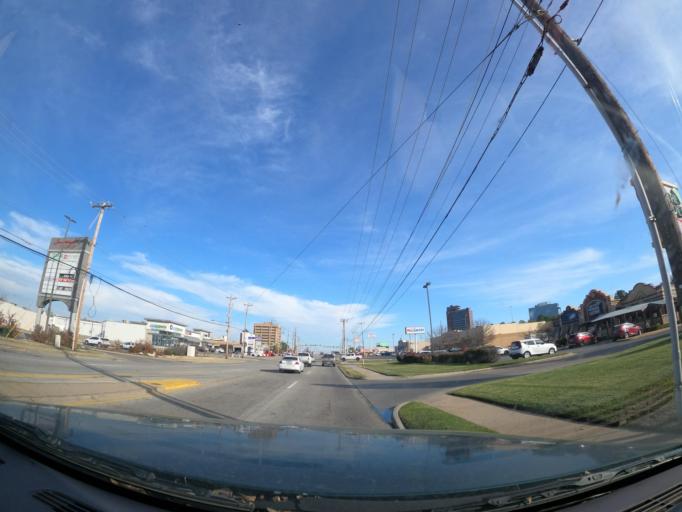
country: US
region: Oklahoma
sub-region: Tulsa County
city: Tulsa
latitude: 36.1044
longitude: -95.9158
